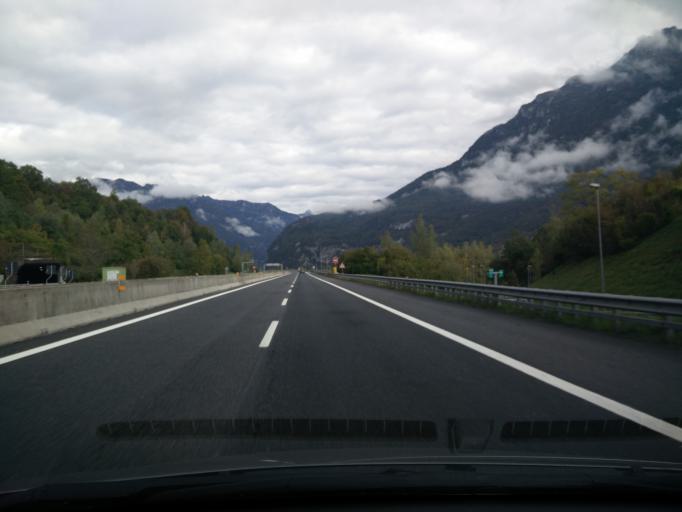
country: IT
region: Veneto
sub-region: Provincia di Belluno
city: Soccher-Paiane-Casan-Arsie
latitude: 46.1652
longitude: 12.3124
